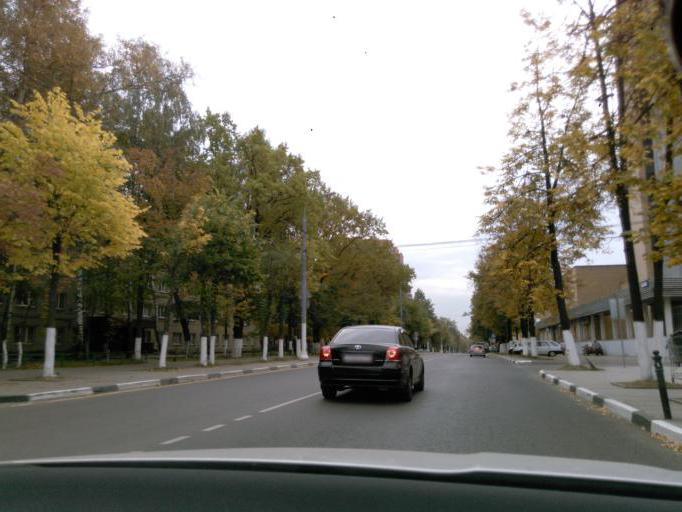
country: RU
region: Moscow
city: Severnyy
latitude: 55.9296
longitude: 37.5217
